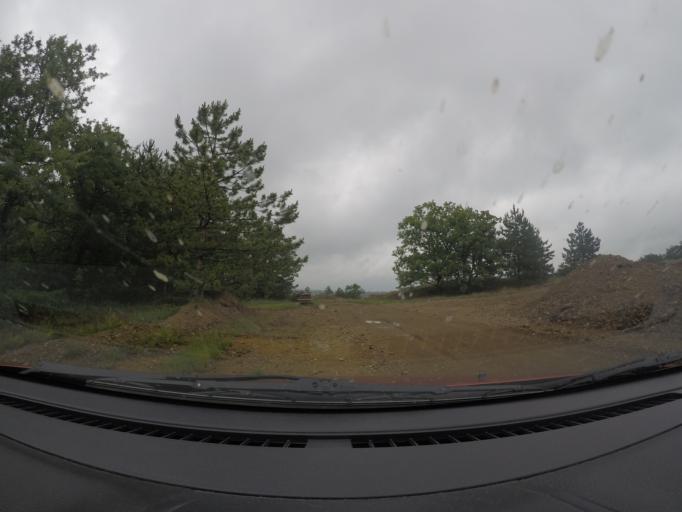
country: RS
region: Central Serbia
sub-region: Belgrade
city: Sopot
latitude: 44.5435
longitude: 20.5099
